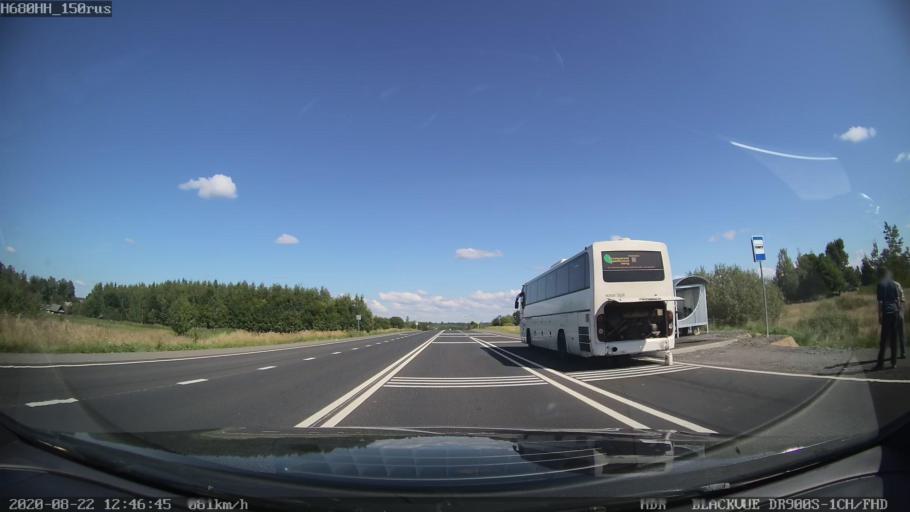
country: RU
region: Tverskaya
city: Rameshki
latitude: 57.4235
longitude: 36.1526
